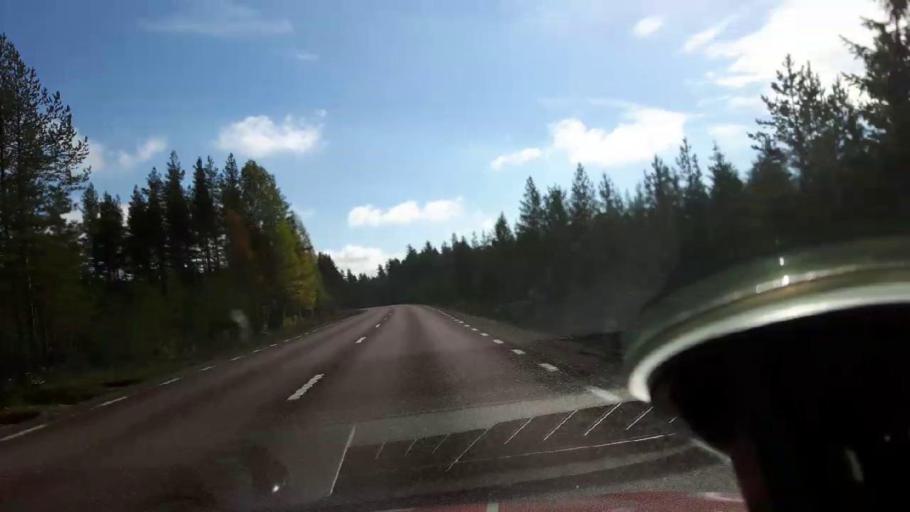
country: SE
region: Gaevleborg
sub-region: Ljusdals Kommun
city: Farila
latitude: 61.9214
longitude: 15.6067
